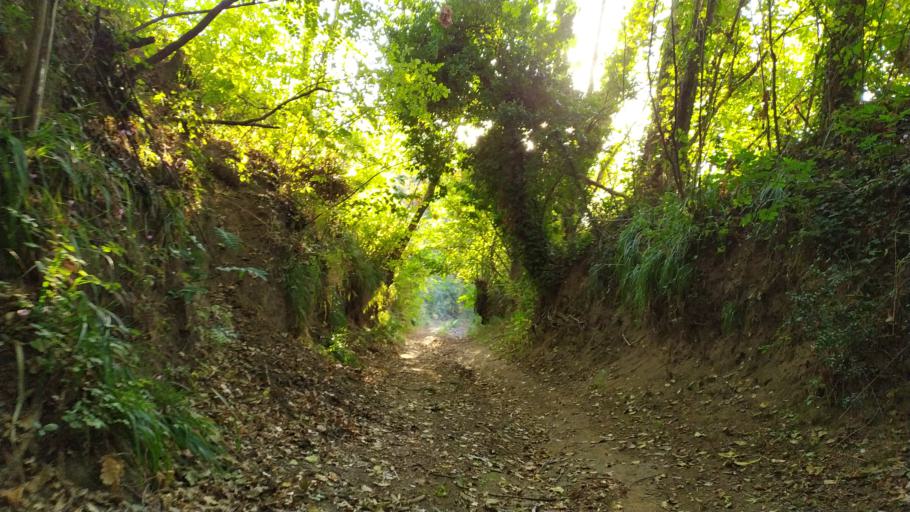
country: IT
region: Campania
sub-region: Provincia di Salerno
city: Lanzara
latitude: 40.7763
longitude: 14.6629
